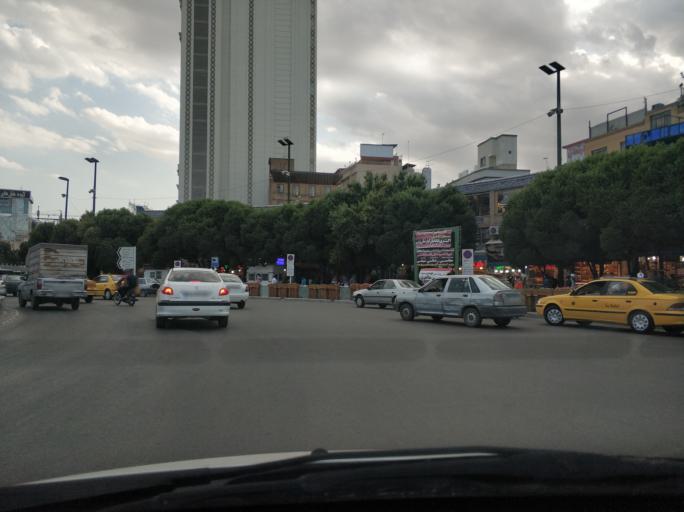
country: IR
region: Razavi Khorasan
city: Mashhad
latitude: 36.2841
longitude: 59.6119
